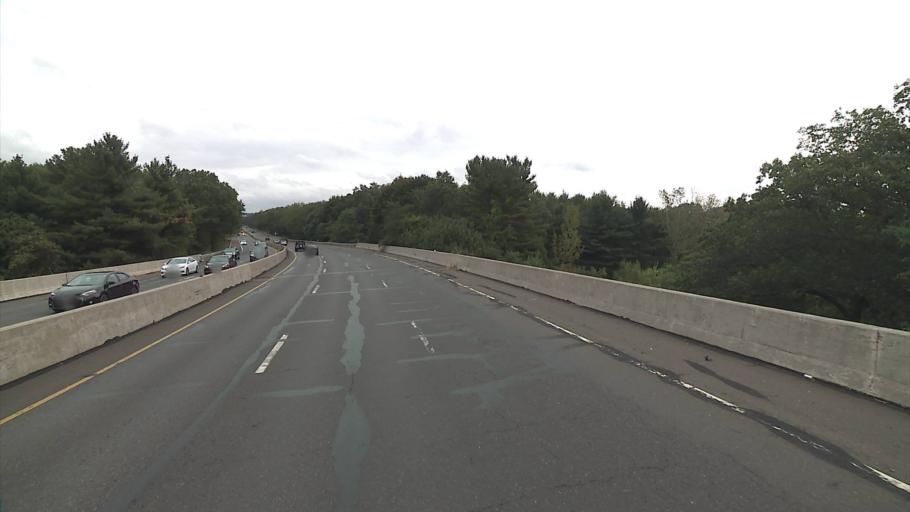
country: US
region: Connecticut
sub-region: New Haven County
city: Hamden
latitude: 41.3665
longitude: -72.9182
